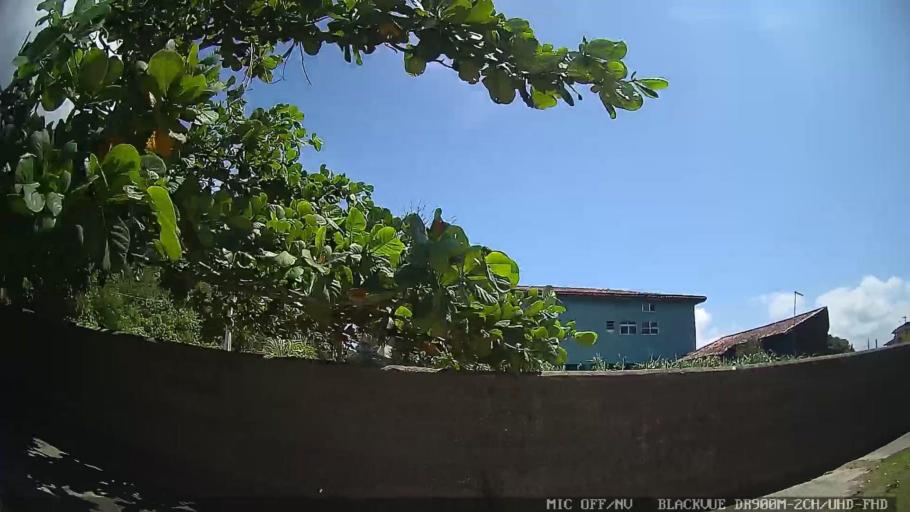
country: BR
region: Sao Paulo
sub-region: Peruibe
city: Peruibe
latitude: -24.3353
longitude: -47.0038
